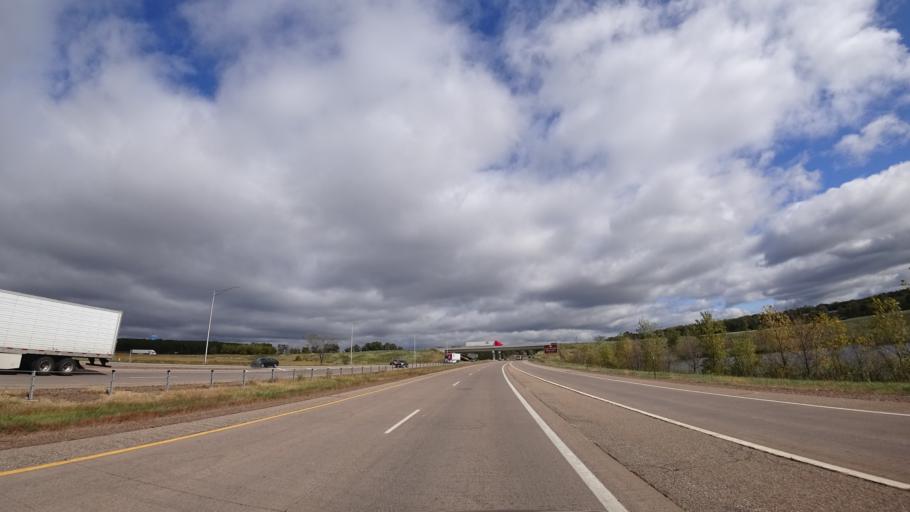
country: US
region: Wisconsin
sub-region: Chippewa County
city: Chippewa Falls
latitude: 44.9195
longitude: -91.3612
